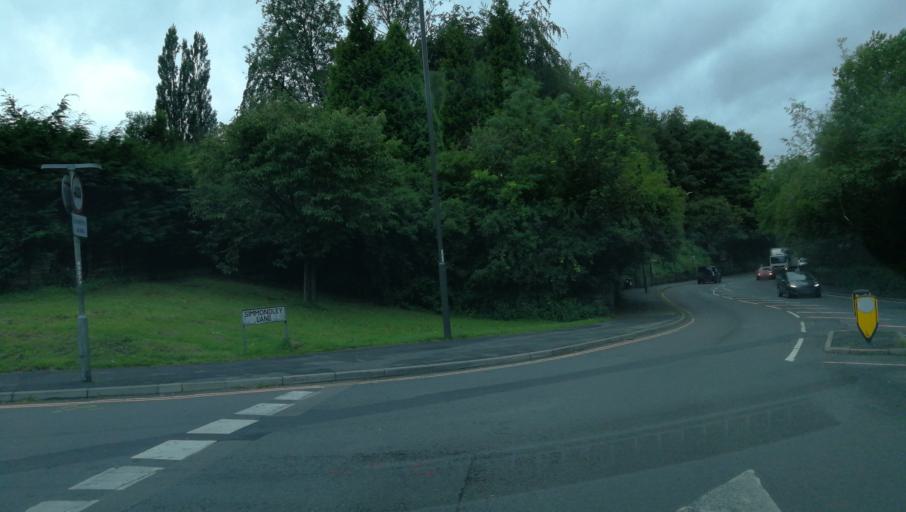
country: GB
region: England
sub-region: Derbyshire
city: Glossop
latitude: 53.4443
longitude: -1.9673
